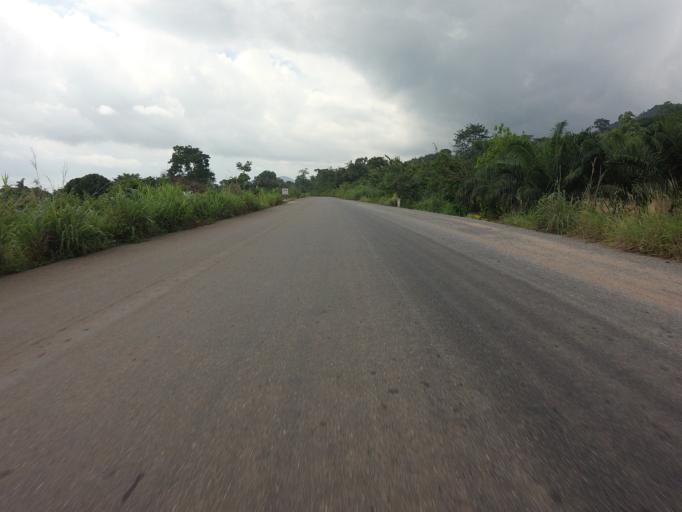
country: GH
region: Volta
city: Kpandu
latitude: 6.9067
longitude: 0.4442
